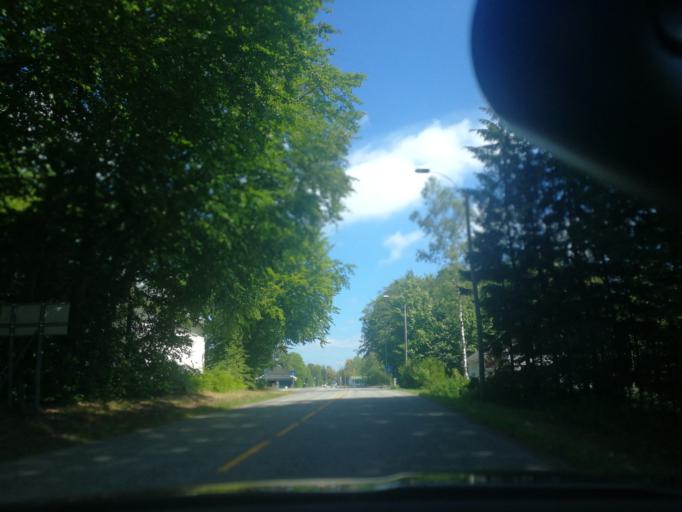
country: NO
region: Vestfold
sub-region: Sandefjord
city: Sandefjord
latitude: 59.1940
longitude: 10.2296
